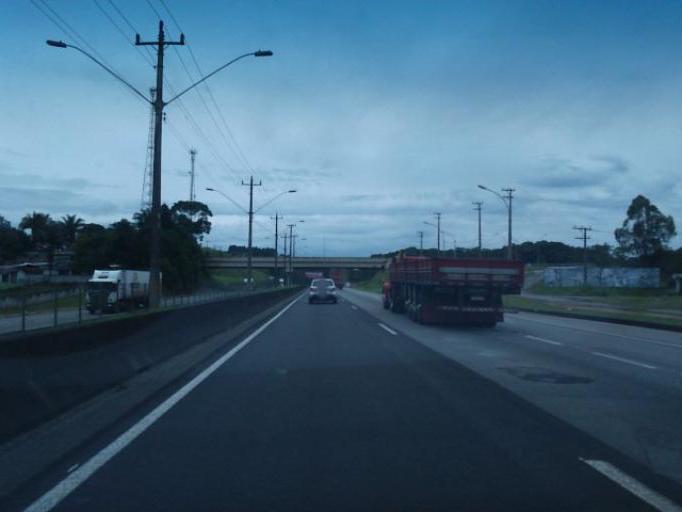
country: BR
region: Sao Paulo
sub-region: Juquitiba
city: Juquitiba
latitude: -23.9234
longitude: -46.9930
